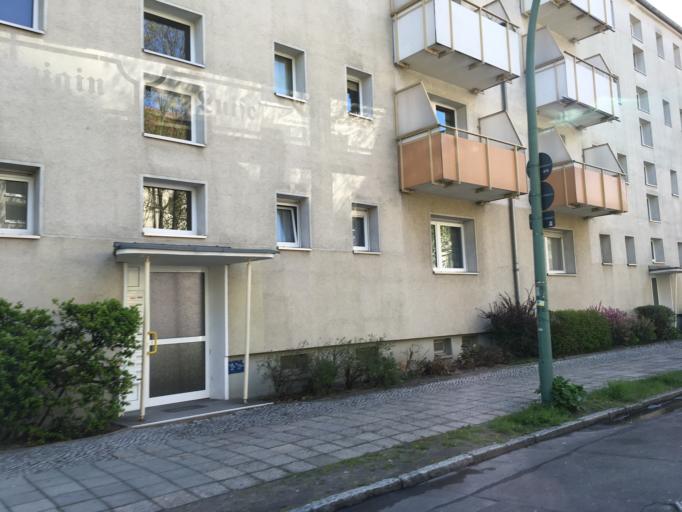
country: DE
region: Brandenburg
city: Potsdam
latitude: 52.4003
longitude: 13.0627
